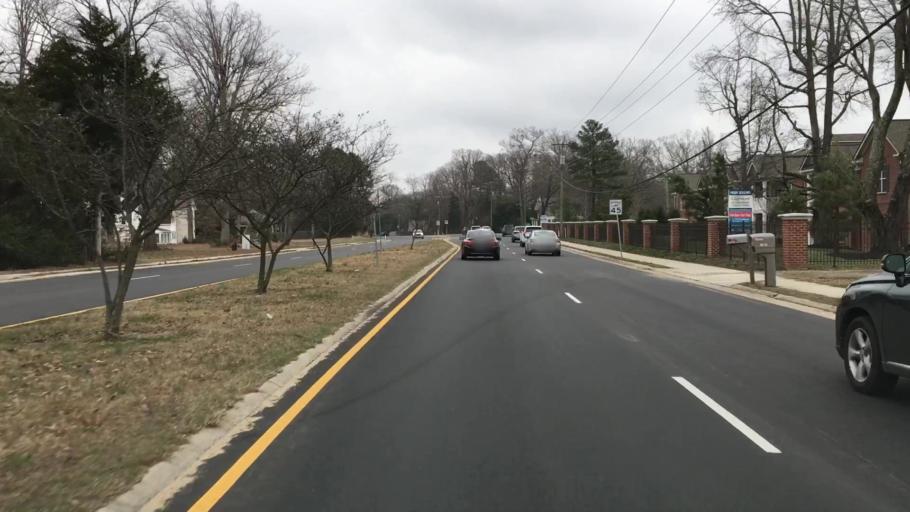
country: US
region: Virginia
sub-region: Chesterfield County
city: Bon Air
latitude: 37.5195
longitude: -77.6043
